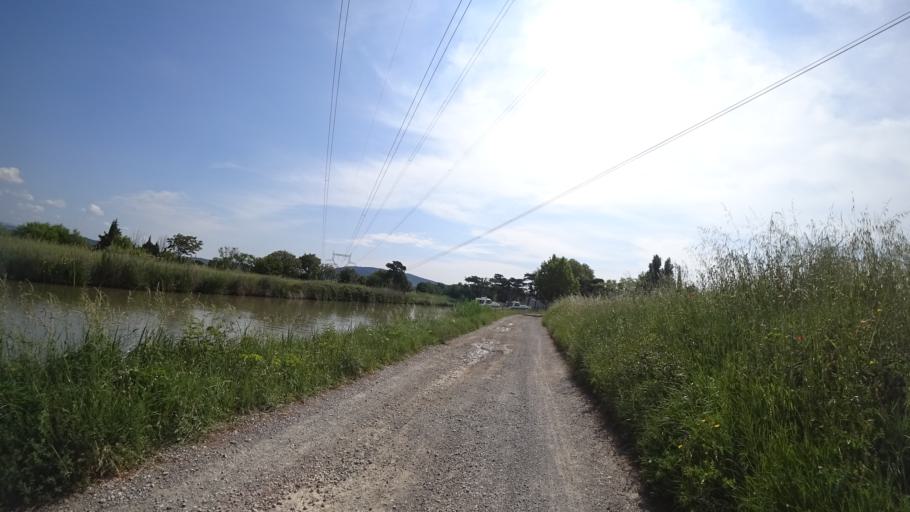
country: FR
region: Languedoc-Roussillon
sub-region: Departement de l'Herault
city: Olonzac
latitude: 43.2699
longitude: 2.7360
